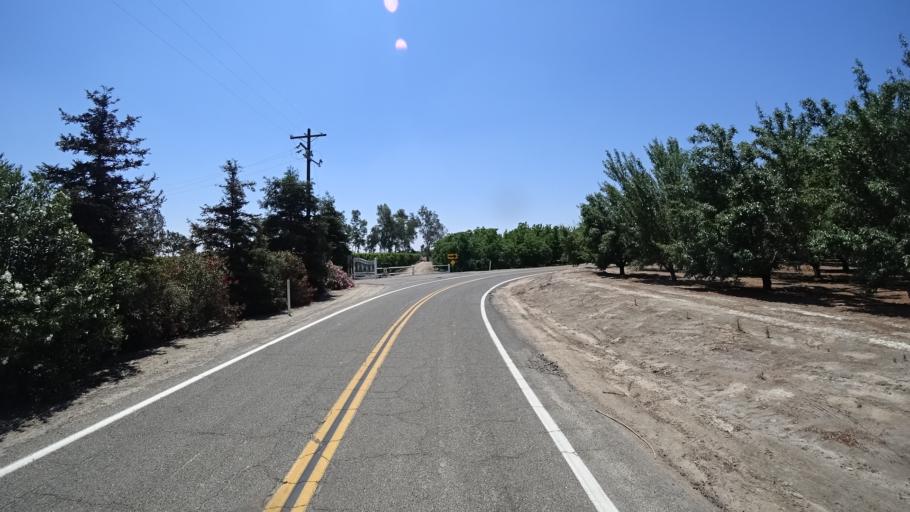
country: US
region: California
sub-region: Fresno County
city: Kingsburg
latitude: 36.4854
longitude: -119.5640
